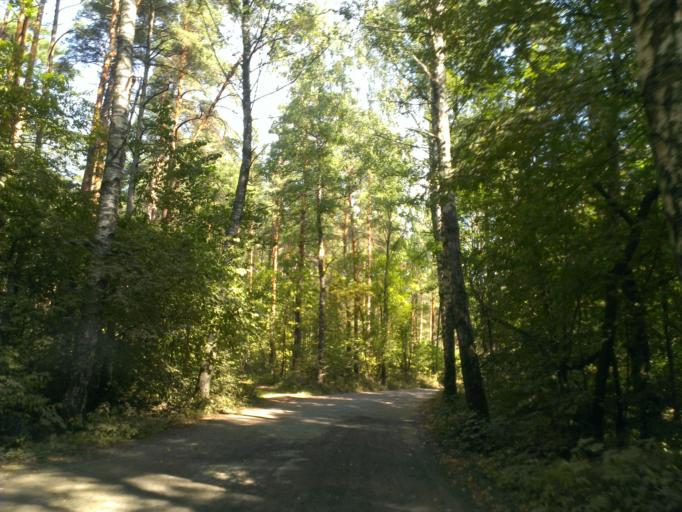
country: LV
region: Adazi
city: Adazi
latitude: 57.0860
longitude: 24.3440
